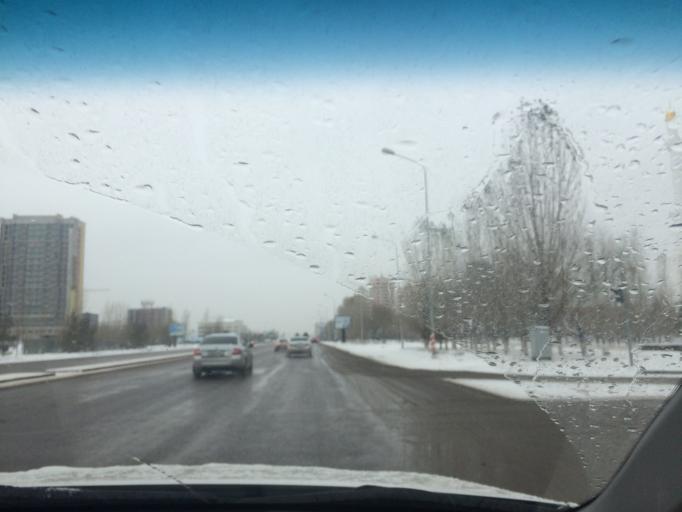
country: KZ
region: Astana Qalasy
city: Astana
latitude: 51.1251
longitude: 71.4173
